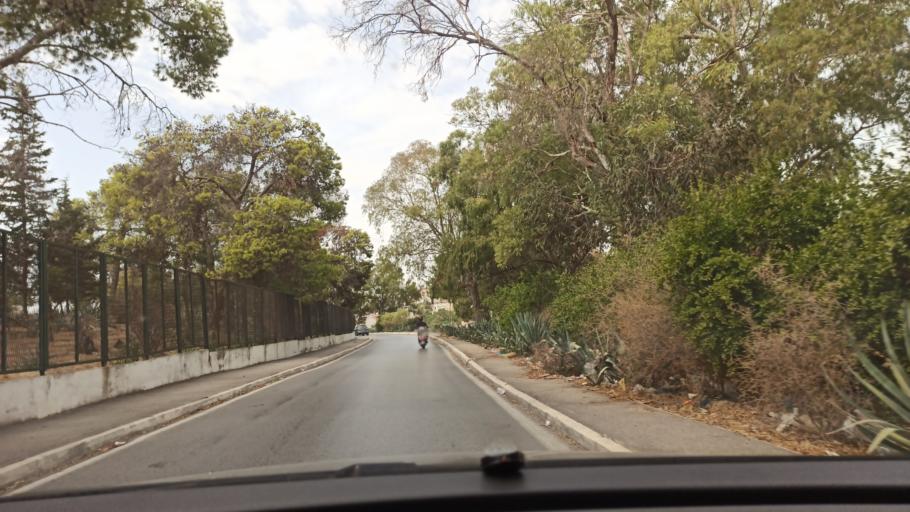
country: TN
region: Tunis
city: Tunis
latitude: 36.8246
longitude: 10.1688
